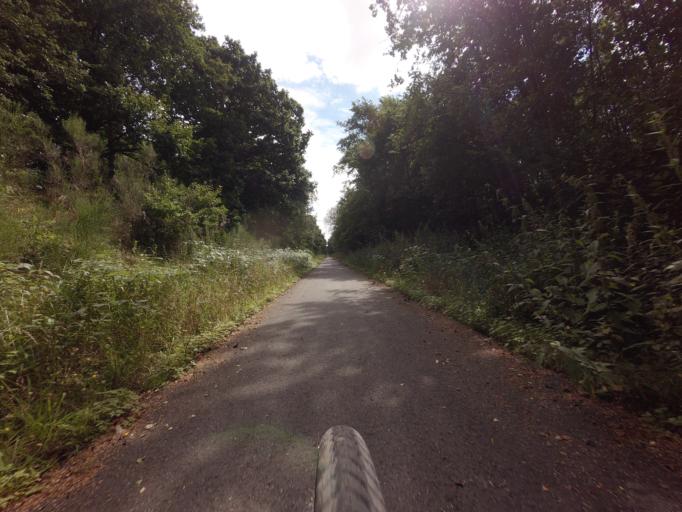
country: DK
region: Central Jutland
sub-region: Norddjurs Kommune
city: Auning
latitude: 56.3989
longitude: 10.4044
